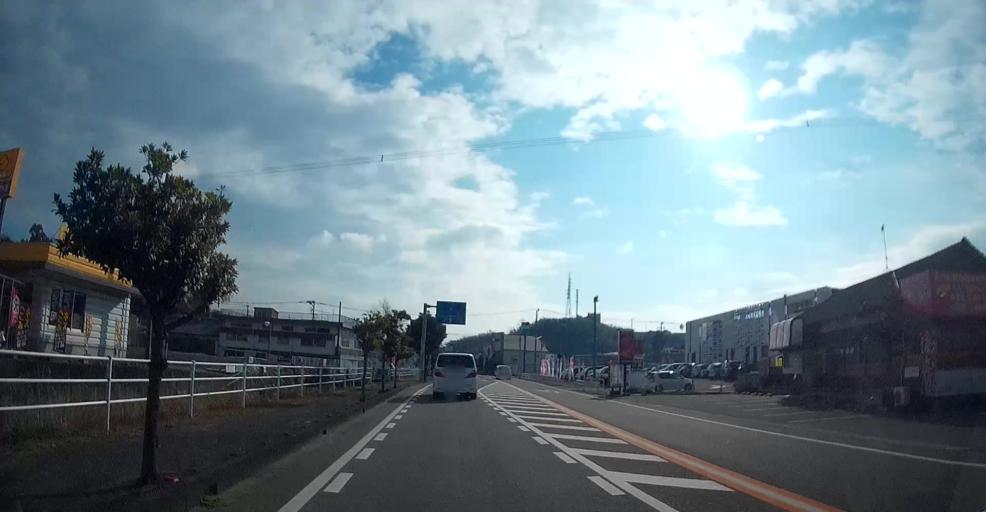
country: JP
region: Kumamoto
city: Yatsushiro
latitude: 32.5904
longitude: 130.4299
